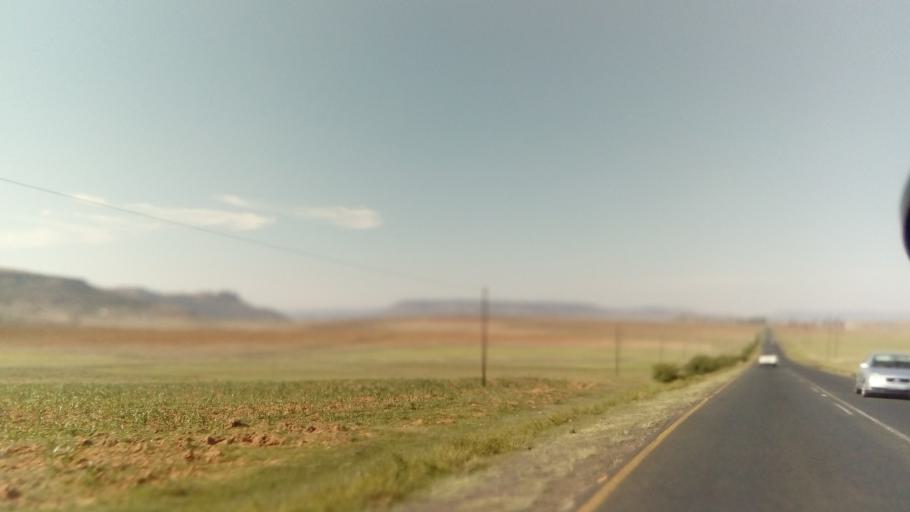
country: LS
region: Berea
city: Teyateyaneng
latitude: -29.1698
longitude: 27.6393
